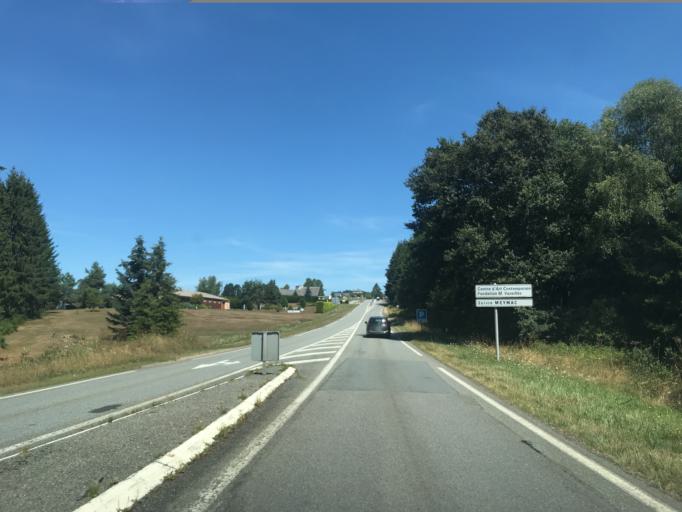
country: FR
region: Limousin
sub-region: Departement de la Correze
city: Meymac
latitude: 45.4630
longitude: 2.1387
